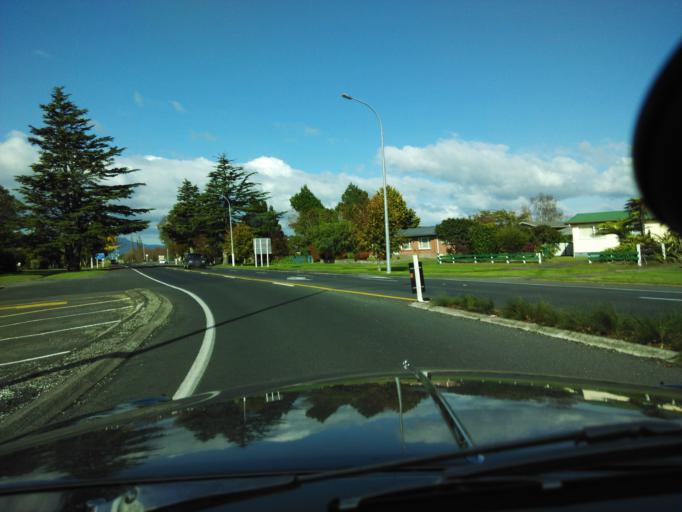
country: NZ
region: Waikato
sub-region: Hauraki District
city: Paeroa
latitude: -37.5502
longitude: 175.7024
